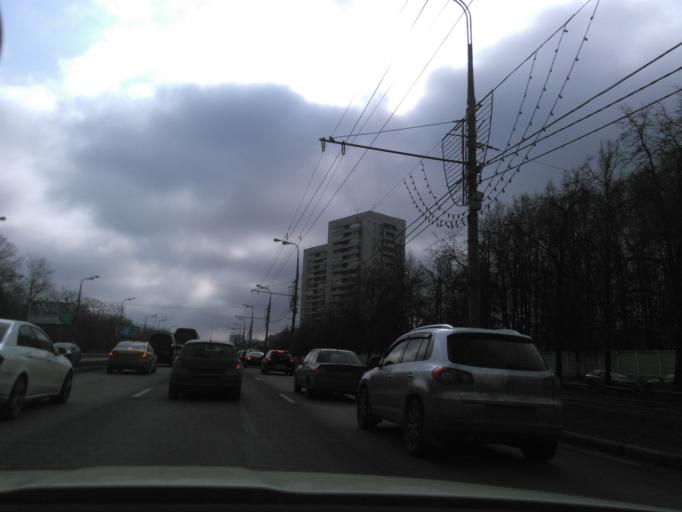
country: RU
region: Moscow
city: Pokrovskoye-Streshnevo
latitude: 55.8155
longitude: 37.4658
